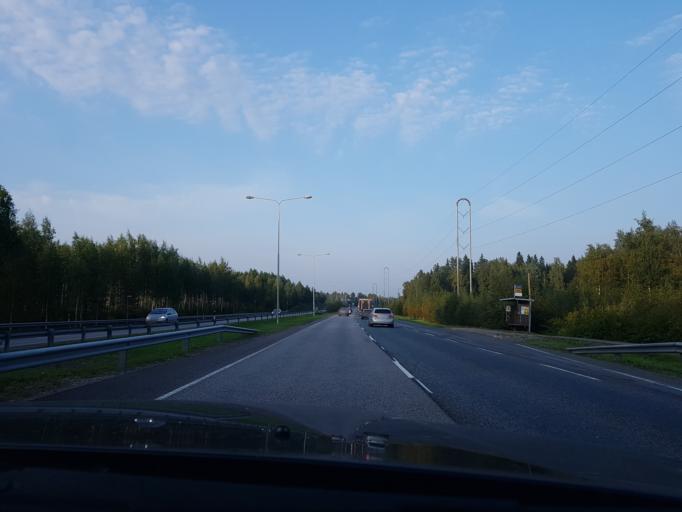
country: FI
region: Uusimaa
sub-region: Helsinki
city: Tuusula
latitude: 60.3684
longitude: 25.0113
